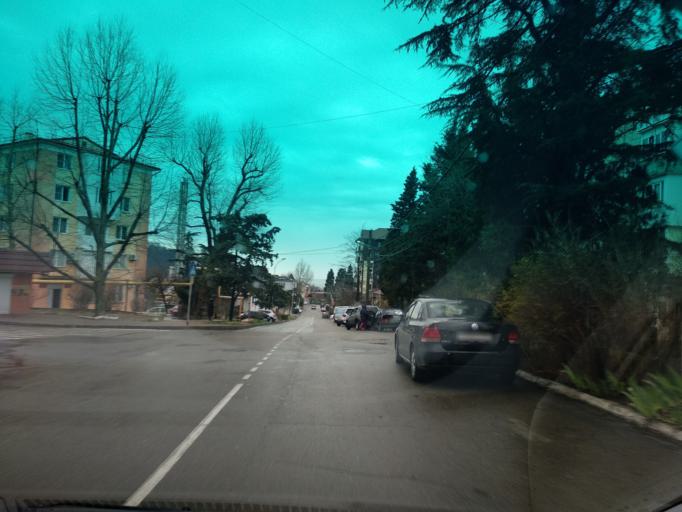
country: RU
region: Krasnodarskiy
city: Tuapse
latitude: 44.1057
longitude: 39.0834
